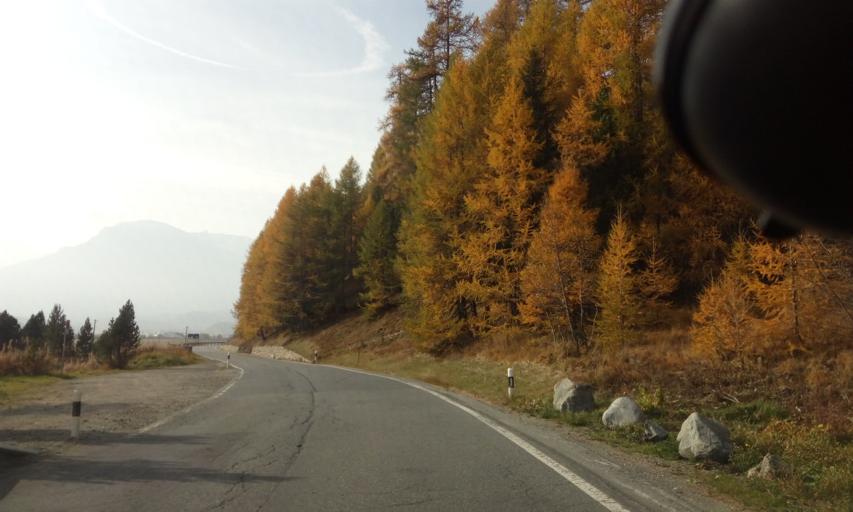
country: CH
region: Grisons
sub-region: Maloja District
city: Samedan
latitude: 46.5445
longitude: 9.8828
